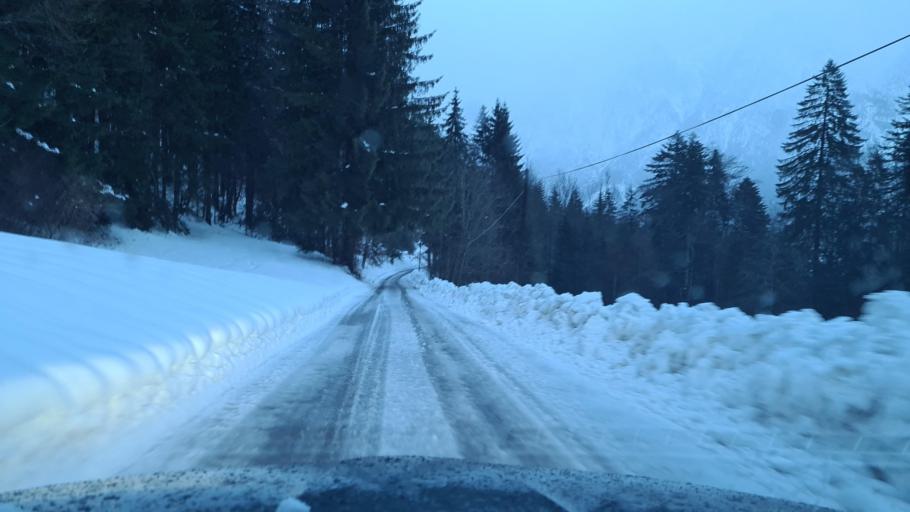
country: AT
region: Salzburg
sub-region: Politischer Bezirk Sankt Johann im Pongau
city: Werfen
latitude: 47.4850
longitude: 13.1559
